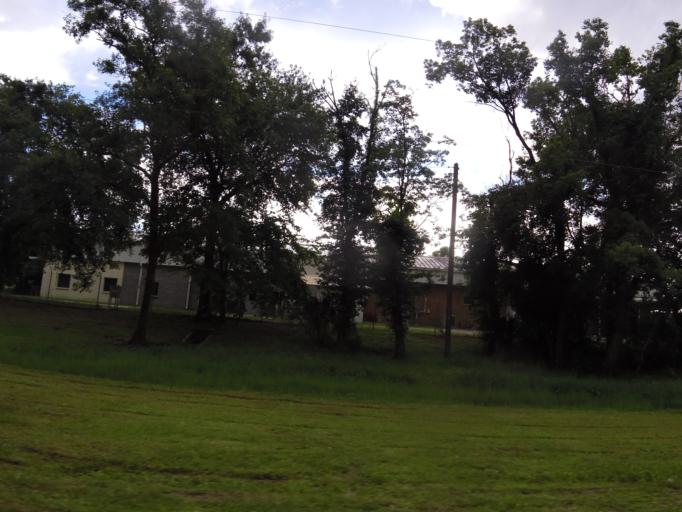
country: US
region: Florida
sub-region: Duval County
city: Jacksonville
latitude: 30.4037
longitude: -81.6618
